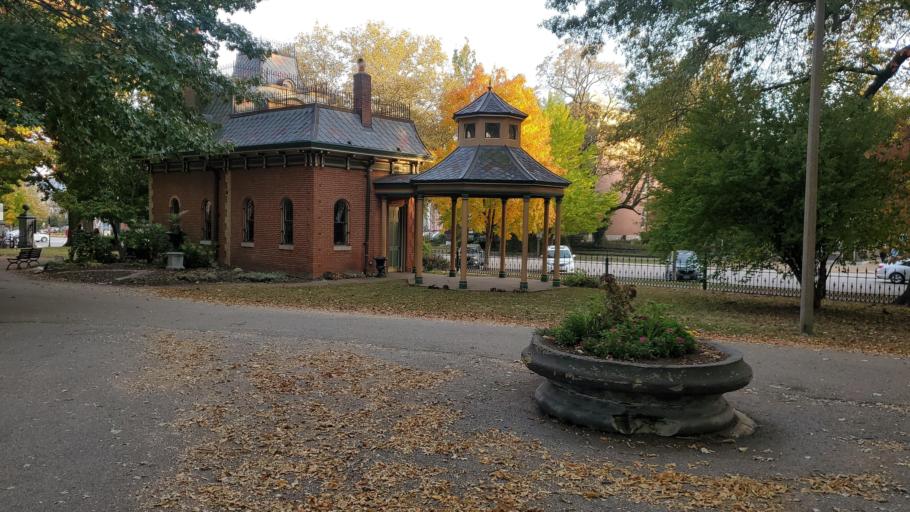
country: US
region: Missouri
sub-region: City of Saint Louis
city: St. Louis
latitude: 38.6145
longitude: -90.2152
